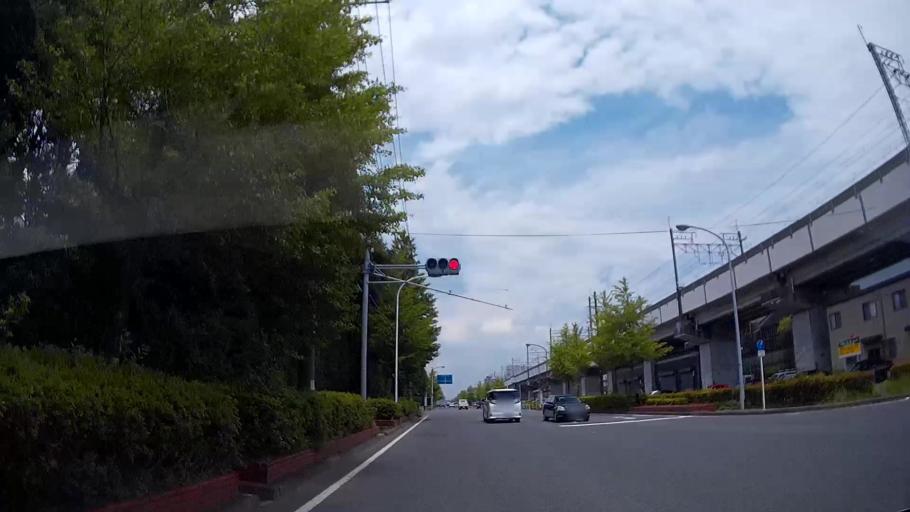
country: JP
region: Tokyo
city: Urayasu
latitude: 35.6394
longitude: 139.8998
